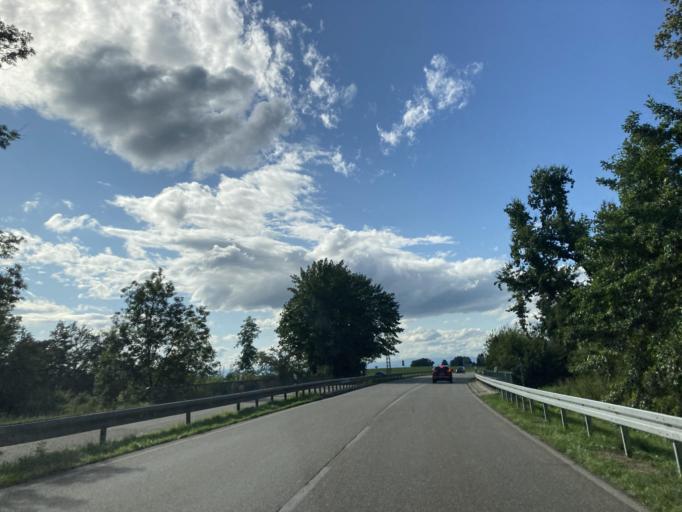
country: DE
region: Baden-Wuerttemberg
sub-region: Freiburg Region
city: Unterkrozingen
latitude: 47.9276
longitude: 7.6920
